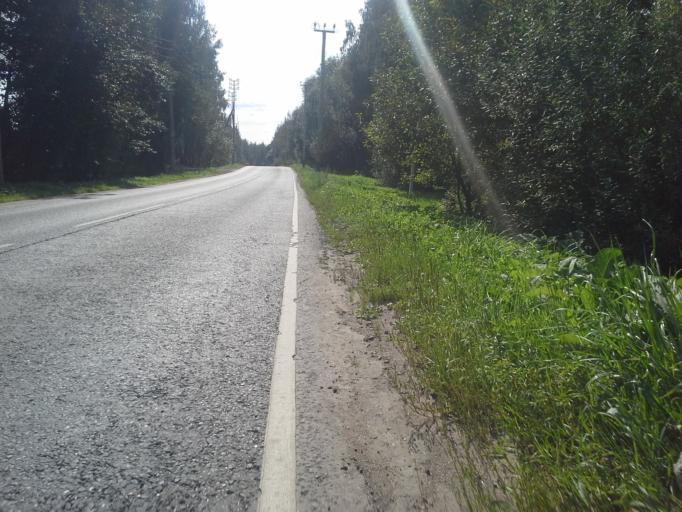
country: RU
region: Moskovskaya
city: Aprelevka
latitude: 55.5743
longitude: 37.1111
